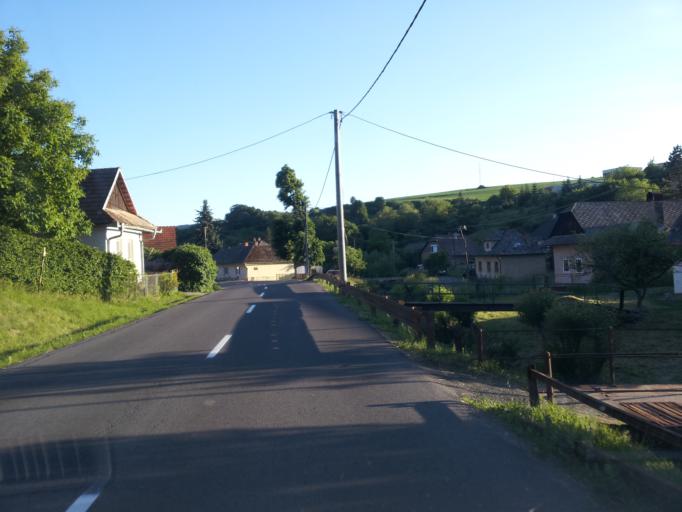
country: SK
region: Banskobystricky
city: Svaety Anton
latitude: 48.4191
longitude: 18.9402
